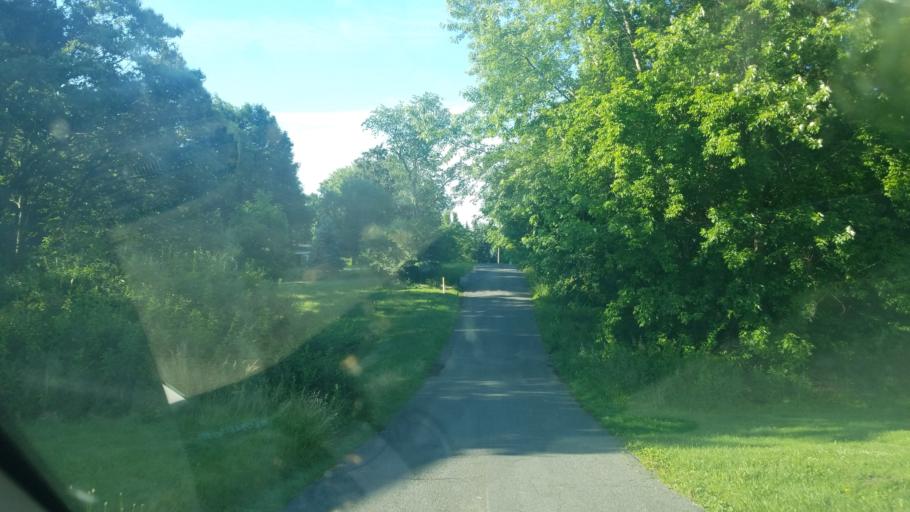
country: US
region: Ohio
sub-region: Columbiana County
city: Salem
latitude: 40.8915
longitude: -80.8725
